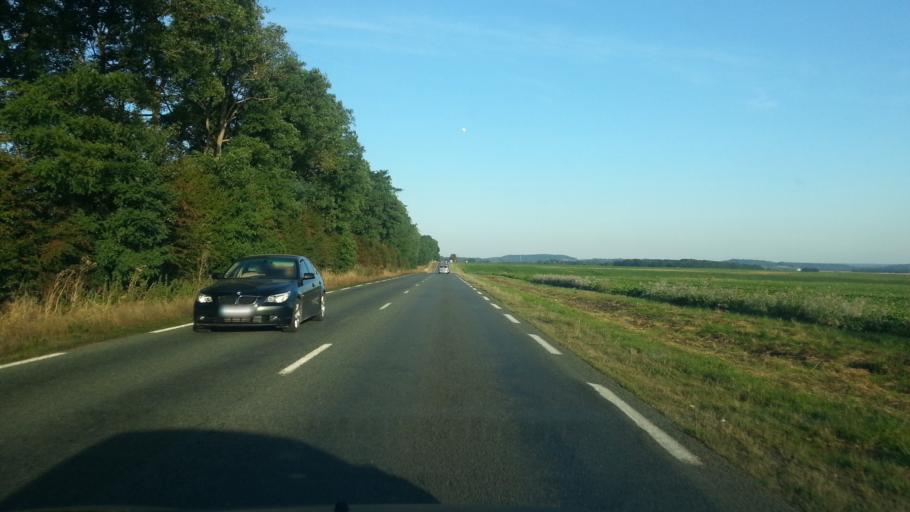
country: FR
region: Picardie
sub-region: Departement de l'Oise
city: Estrees-Saint-Denis
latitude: 49.4037
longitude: 2.6315
